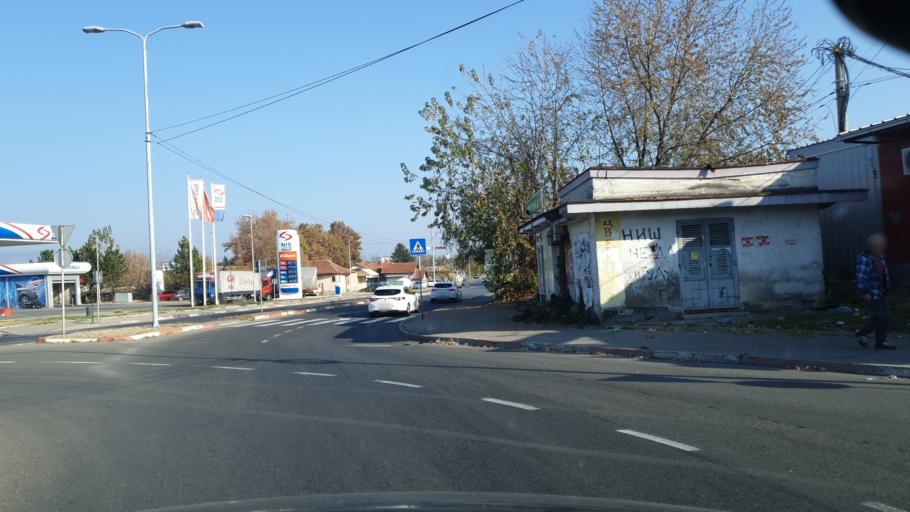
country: RS
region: Central Serbia
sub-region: Nisavski Okrug
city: Nis
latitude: 43.3151
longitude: 21.8641
